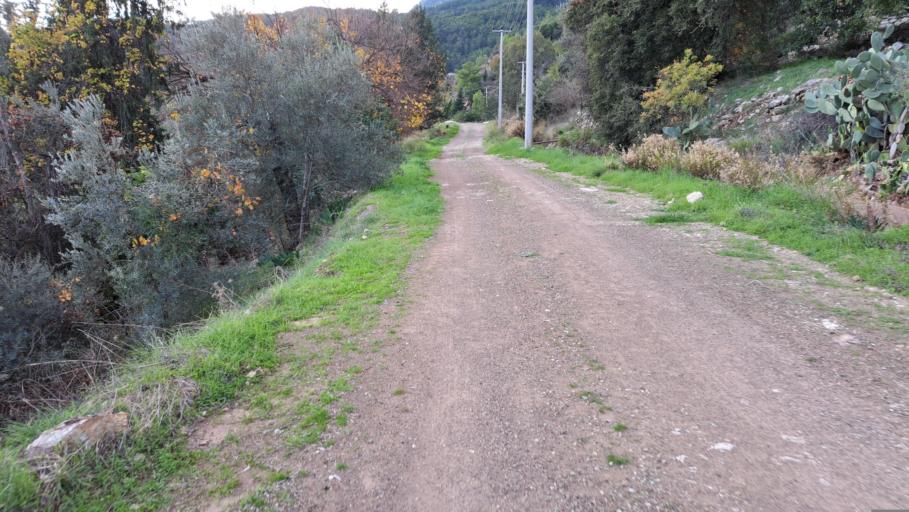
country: TR
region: Antalya
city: Tekirova
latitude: 36.3999
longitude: 30.4350
